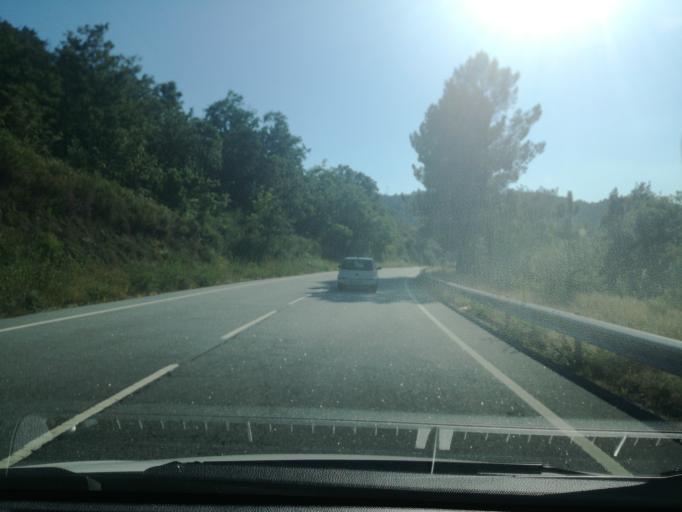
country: ES
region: Galicia
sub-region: Provincia de Ourense
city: Entrimo
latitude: 41.8715
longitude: -8.1759
